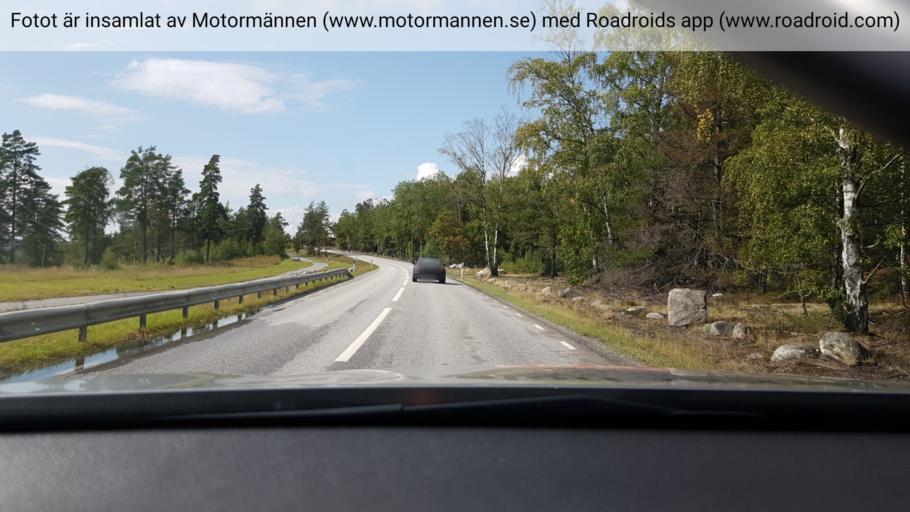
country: SE
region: Stockholm
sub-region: Ekero Kommun
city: Ekeroe
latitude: 59.2773
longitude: 17.7659
